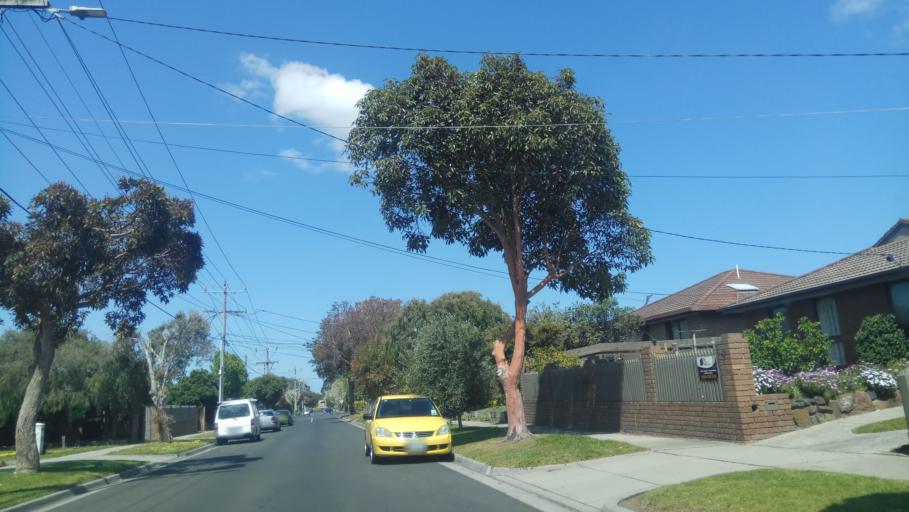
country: AU
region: Victoria
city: Heatherton
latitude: -37.9676
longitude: 145.0829
